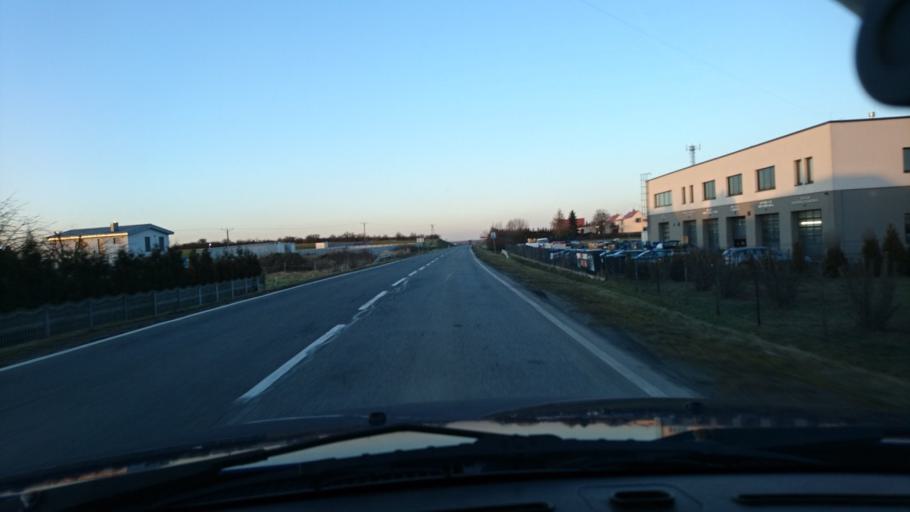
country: PL
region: Silesian Voivodeship
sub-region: Powiat gliwicki
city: Wielowies
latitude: 50.5048
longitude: 18.6045
